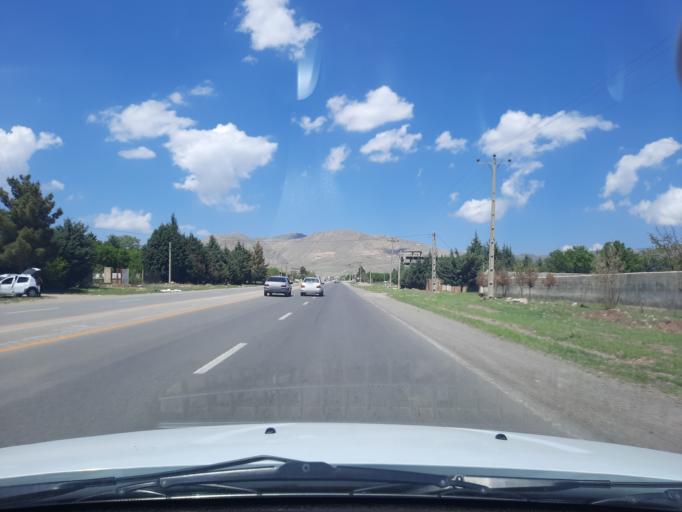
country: IR
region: Qazvin
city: Qazvin
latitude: 36.3179
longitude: 50.1466
